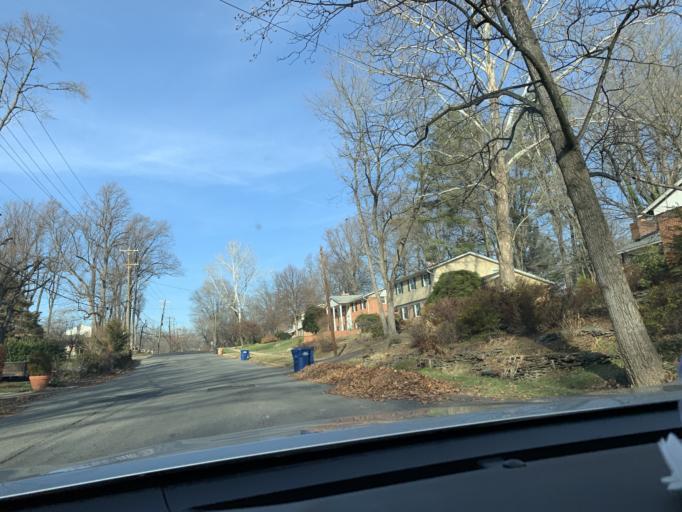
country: US
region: Virginia
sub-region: Fairfax County
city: Jefferson
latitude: 38.8502
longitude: -77.1853
